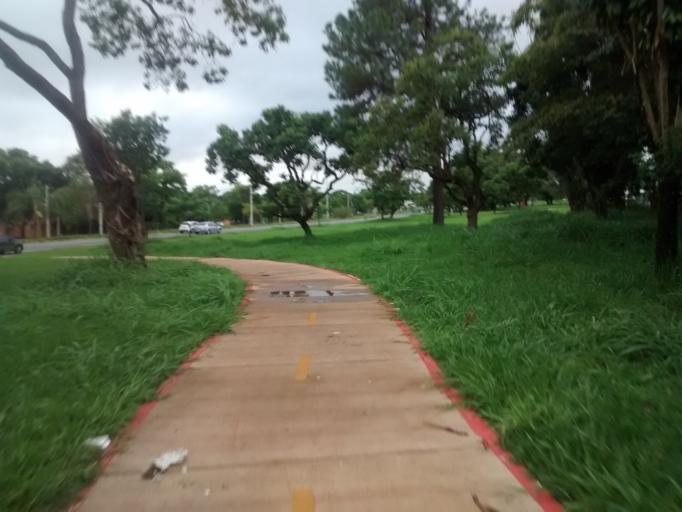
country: BR
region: Federal District
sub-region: Brasilia
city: Brasilia
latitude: -15.7622
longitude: -47.8750
